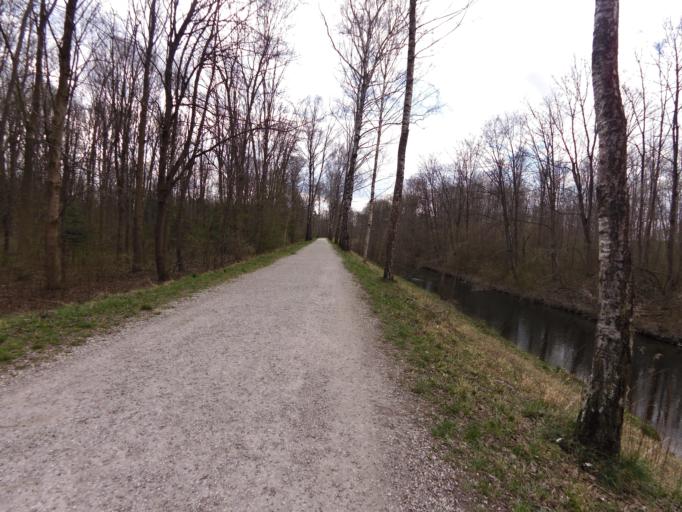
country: DE
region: Bavaria
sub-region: Lower Bavaria
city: Tiefenbach
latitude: 48.5240
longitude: 12.1125
